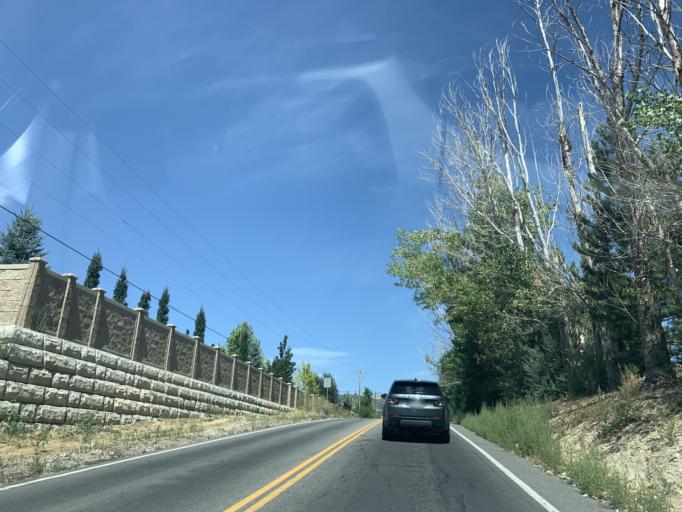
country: US
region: Utah
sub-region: Utah County
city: Lehi
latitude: 40.4246
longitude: -111.8305
